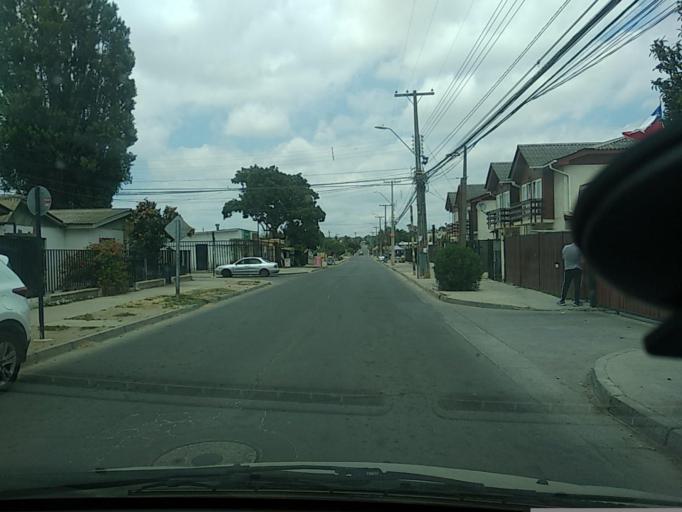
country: CL
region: Valparaiso
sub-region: Provincia de Marga Marga
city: Villa Alemana
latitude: -33.0389
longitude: -71.4077
